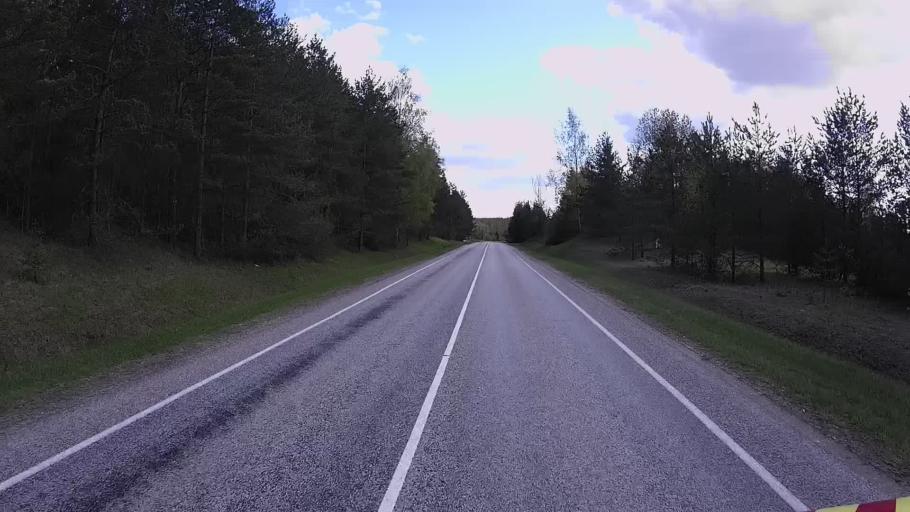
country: EE
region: Jogevamaa
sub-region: Jogeva linn
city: Jogeva
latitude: 58.7801
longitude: 26.4738
